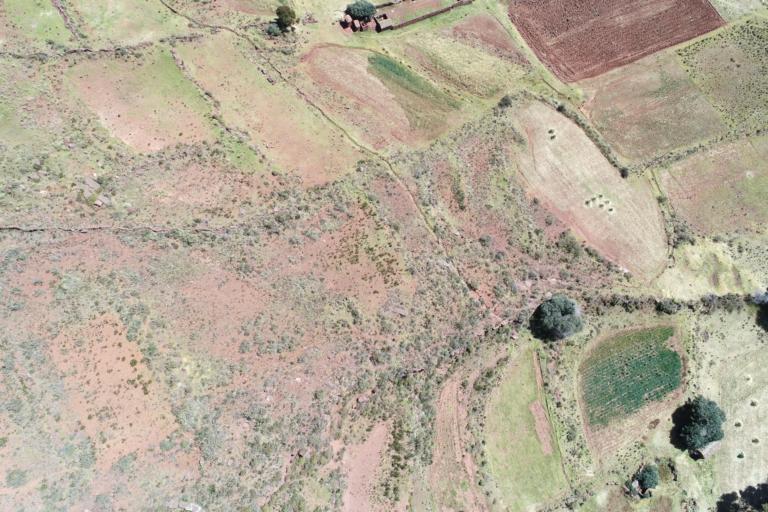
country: BO
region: La Paz
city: Tiahuanaco
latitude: -16.6034
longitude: -68.7706
